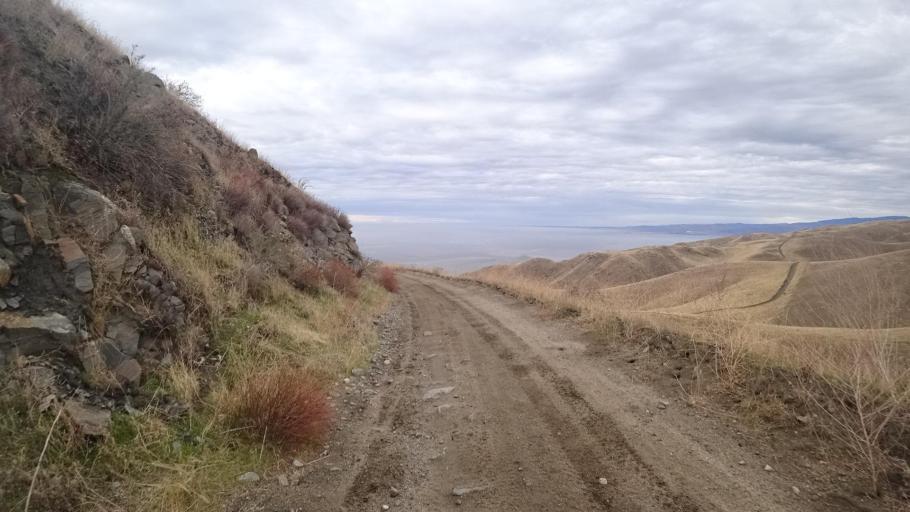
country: US
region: California
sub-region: Kern County
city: Arvin
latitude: 35.1348
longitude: -118.7719
